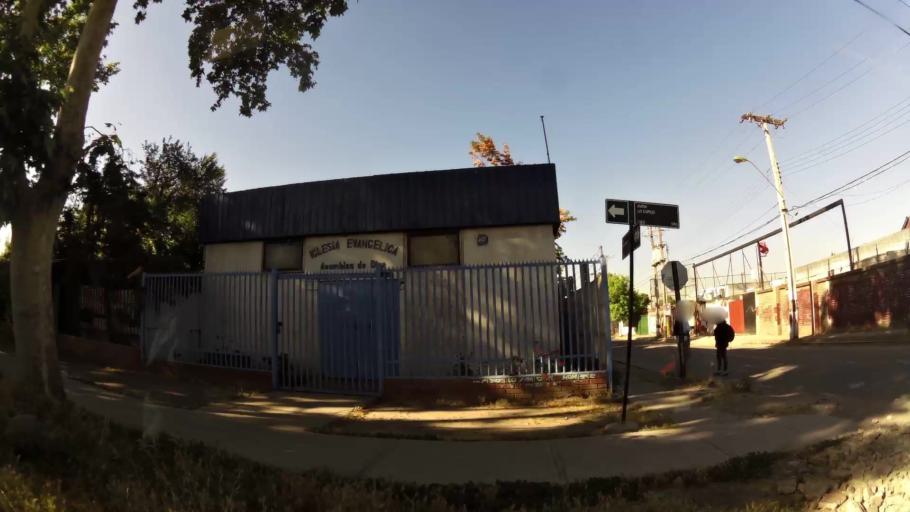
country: CL
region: Santiago Metropolitan
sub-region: Provincia de Maipo
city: San Bernardo
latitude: -33.5414
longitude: -70.6793
